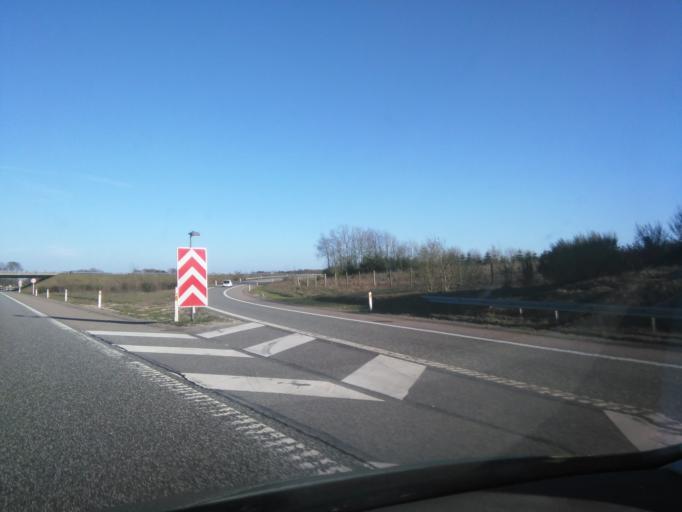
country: DK
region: Central Jutland
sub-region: Herning Kommune
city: Lind
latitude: 56.1117
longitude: 9.0068
